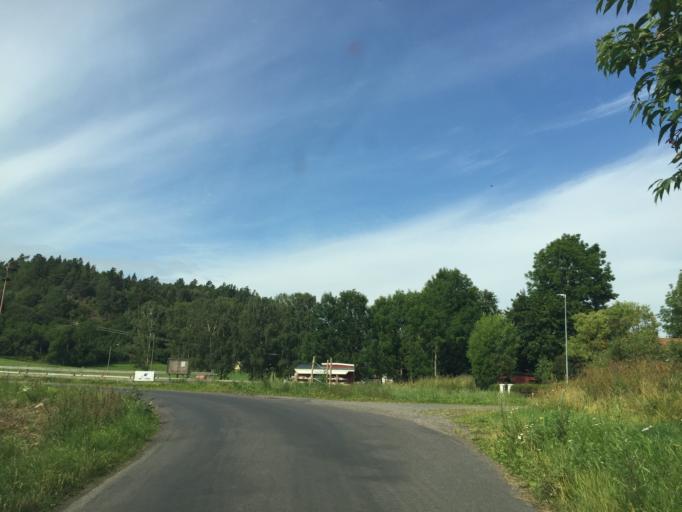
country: SE
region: Joenkoeping
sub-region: Jonkopings Kommun
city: Kaxholmen
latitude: 57.8567
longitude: 14.2821
